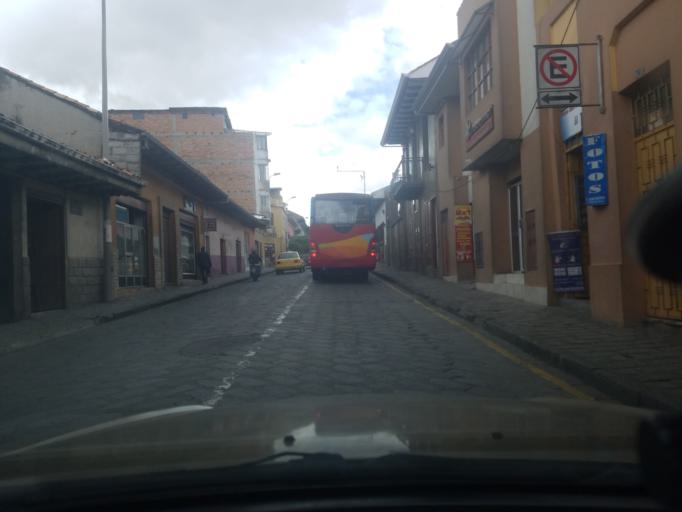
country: EC
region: Azuay
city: Cuenca
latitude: -2.8999
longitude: -79.0008
